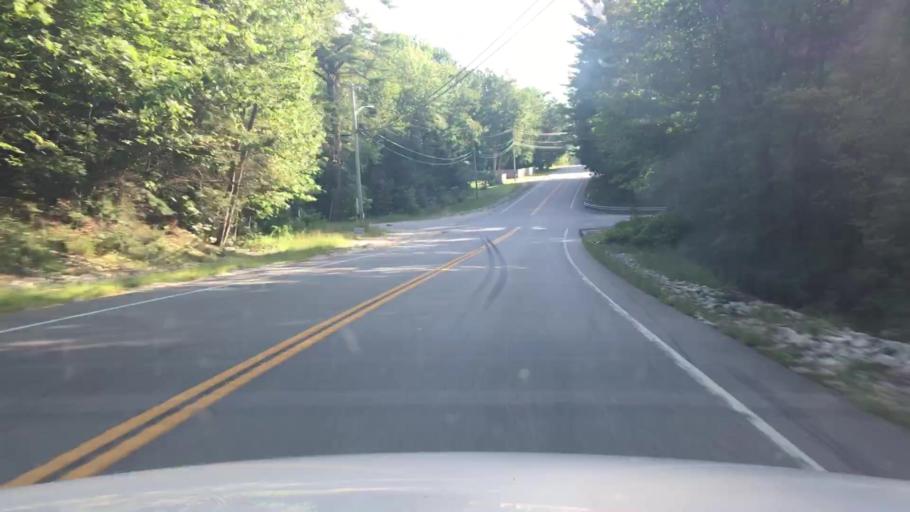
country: US
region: Maine
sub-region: Cumberland County
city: New Gloucester
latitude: 43.9365
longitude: -70.3052
